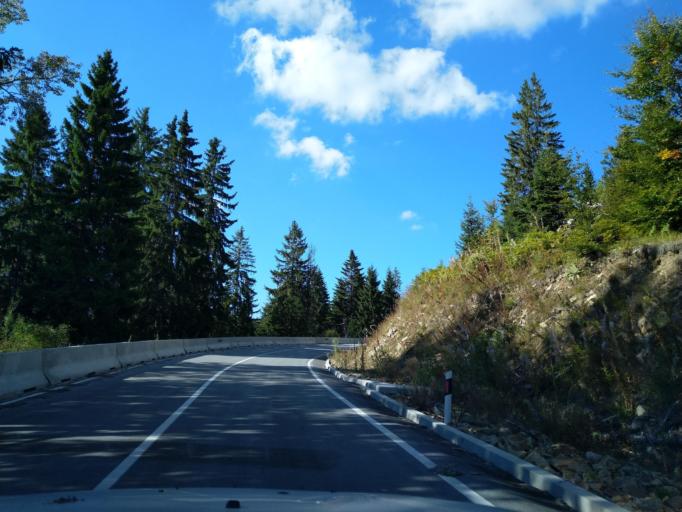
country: RS
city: Sokolovica
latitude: 43.3038
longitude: 20.3050
